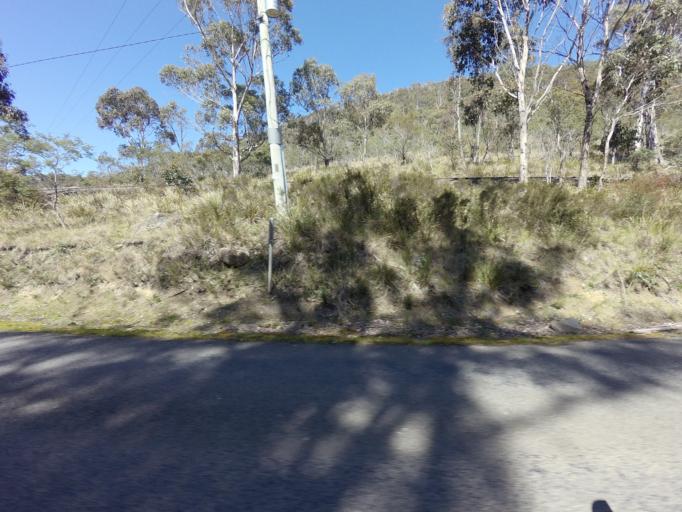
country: AU
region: Tasmania
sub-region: Derwent Valley
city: New Norfolk
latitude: -42.6809
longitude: 146.7462
